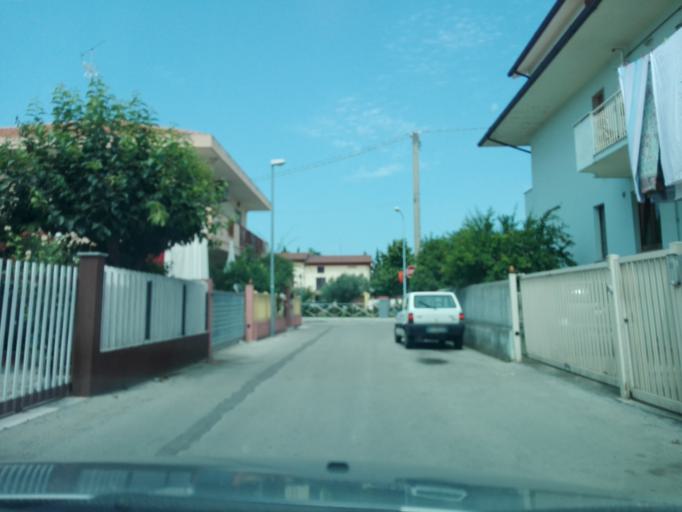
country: IT
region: Abruzzo
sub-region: Provincia di Pescara
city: Montesilvano Marina
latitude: 42.5081
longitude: 14.1395
